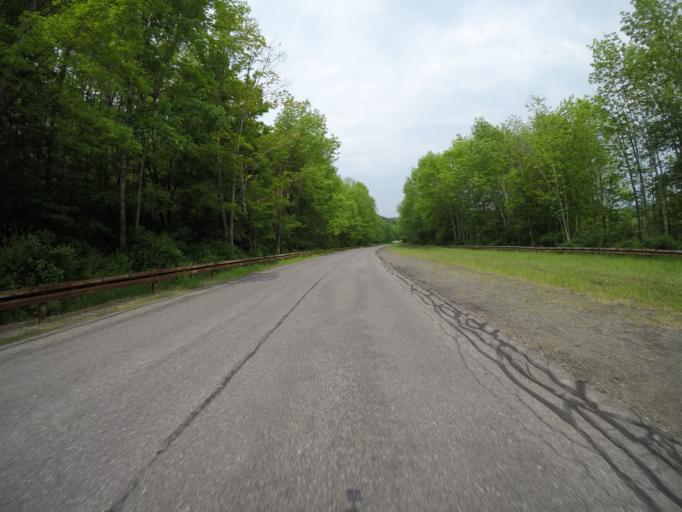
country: US
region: New York
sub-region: Sullivan County
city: Livingston Manor
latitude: 42.0847
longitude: -74.8168
